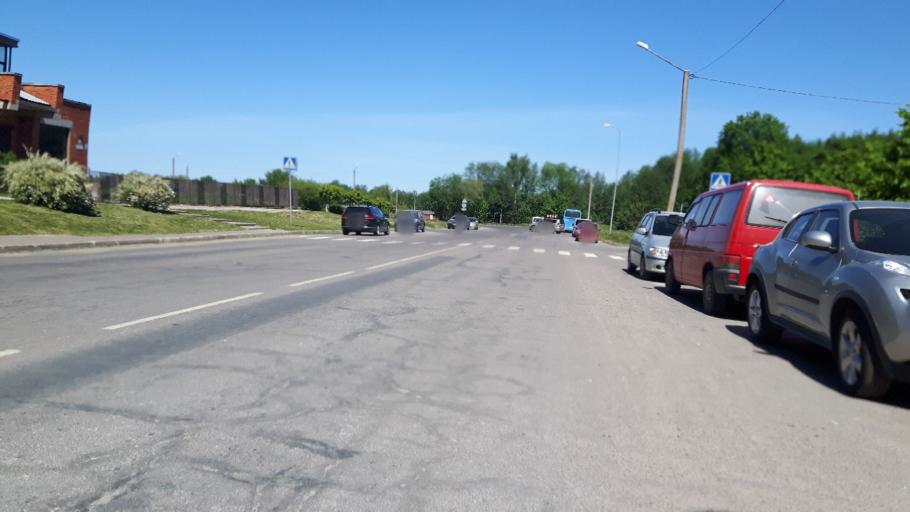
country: EE
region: Ida-Virumaa
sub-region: Sillamaee linn
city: Sillamae
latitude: 59.3930
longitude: 27.7973
